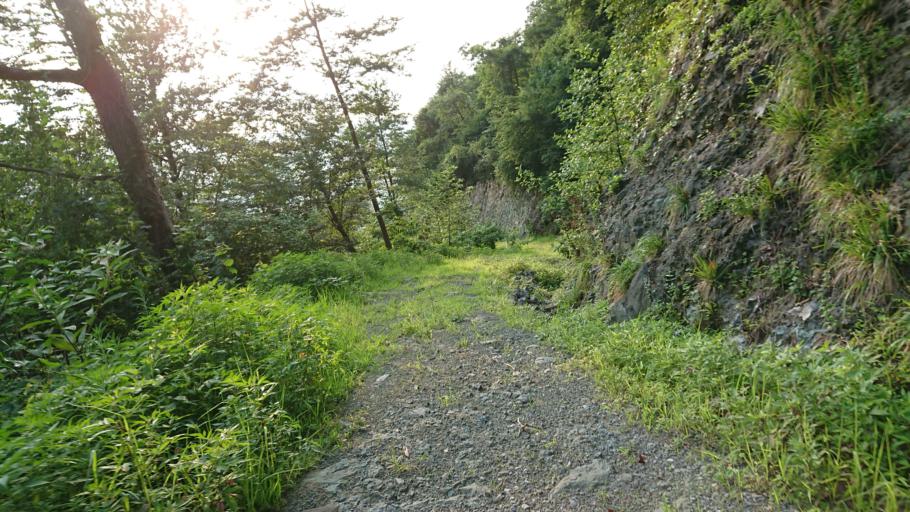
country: TR
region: Rize
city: Rize
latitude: 40.9904
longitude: 40.5030
